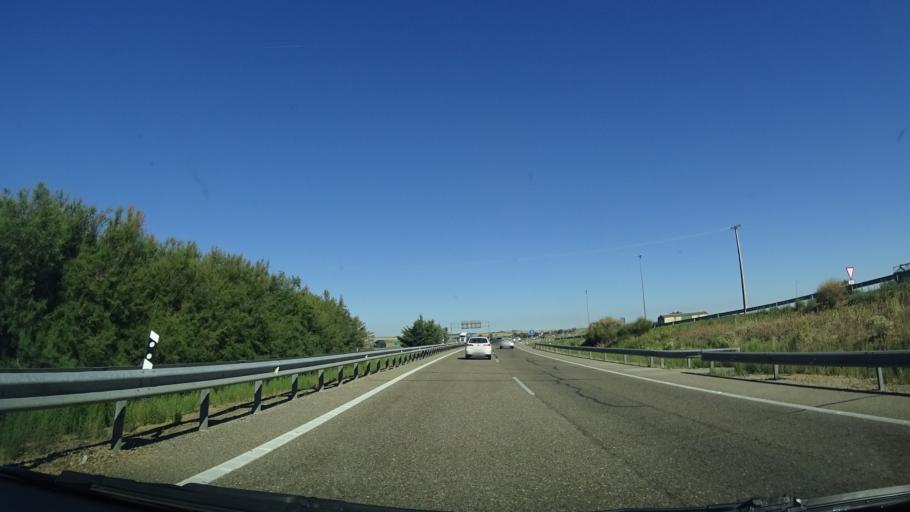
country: ES
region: Castille and Leon
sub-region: Provincia de Zamora
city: Villalpando
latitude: 41.8571
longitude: -5.4230
